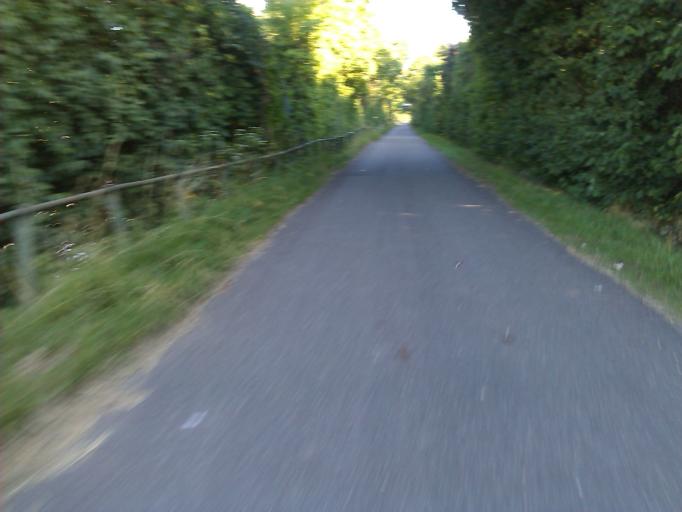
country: DE
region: Baden-Wuerttemberg
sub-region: Regierungsbezirk Stuttgart
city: Neckarsulm
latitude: 49.1945
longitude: 9.2163
